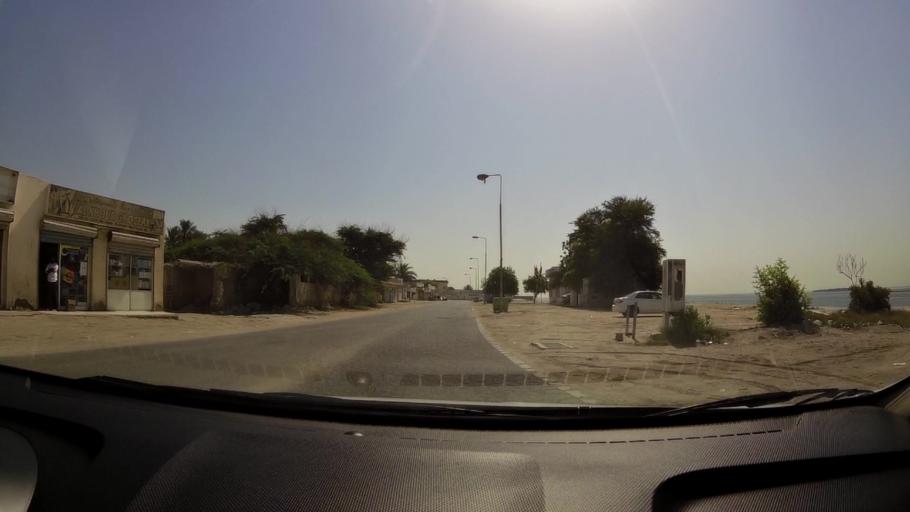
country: AE
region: Umm al Qaywayn
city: Umm al Qaywayn
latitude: 25.5820
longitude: 55.5758
